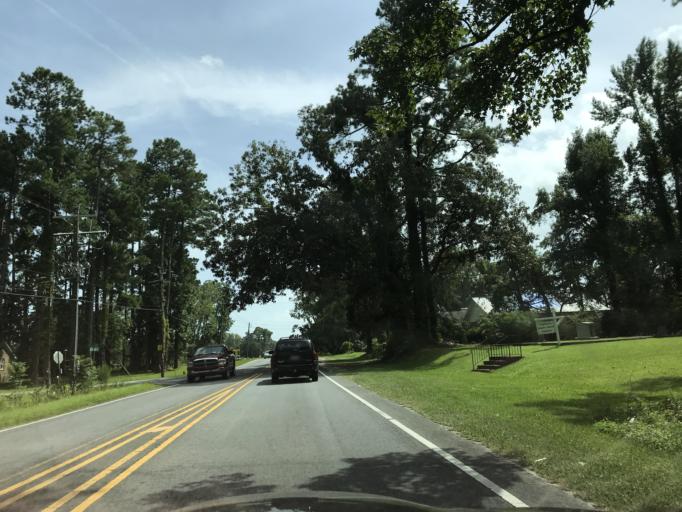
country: US
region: North Carolina
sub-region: New Hanover County
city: Wrightsboro
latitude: 34.3007
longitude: -77.9217
